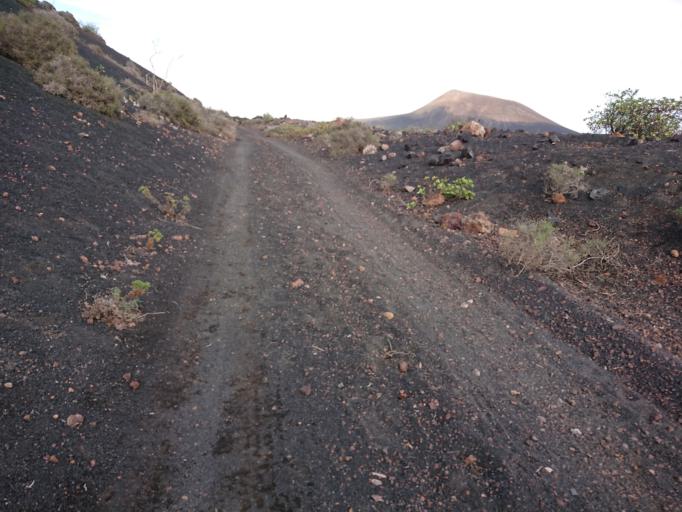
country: ES
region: Canary Islands
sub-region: Provincia de Las Palmas
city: Tinajo
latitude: 29.0115
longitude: -13.6939
